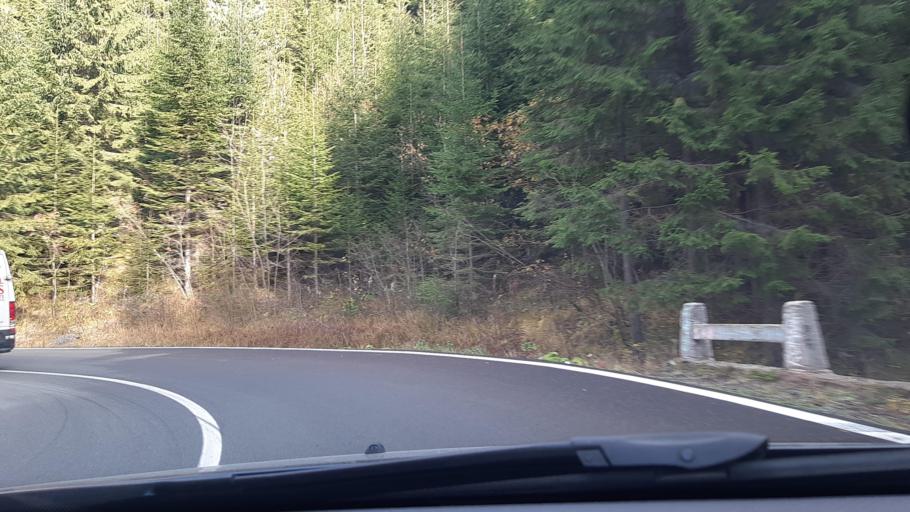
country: RO
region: Valcea
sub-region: Comuna Voineasa
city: Voineasa
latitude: 45.4184
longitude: 23.7409
